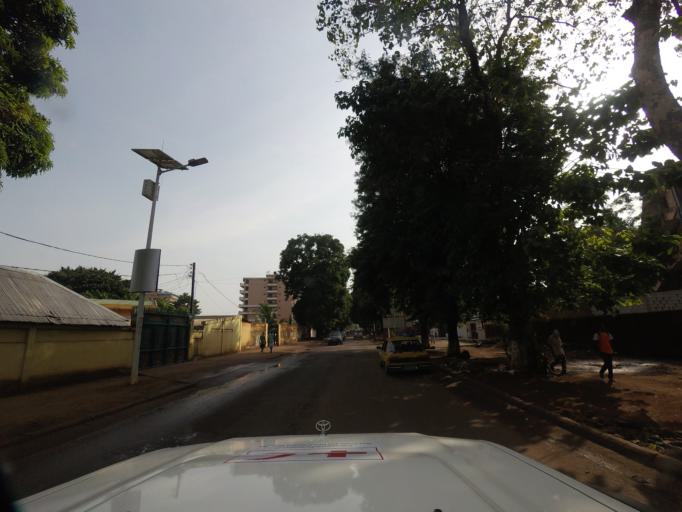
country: GN
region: Conakry
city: Conakry
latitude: 9.5406
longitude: -13.6815
